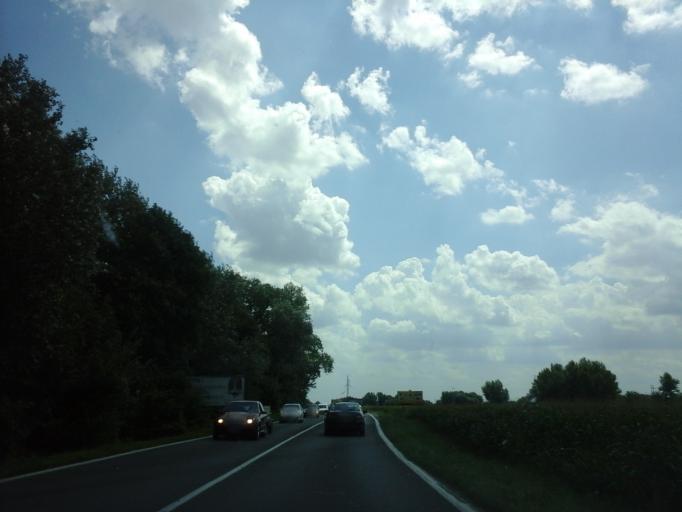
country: AT
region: Burgenland
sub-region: Politischer Bezirk Neusiedl am See
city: Kittsee
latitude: 48.0839
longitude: 17.1250
